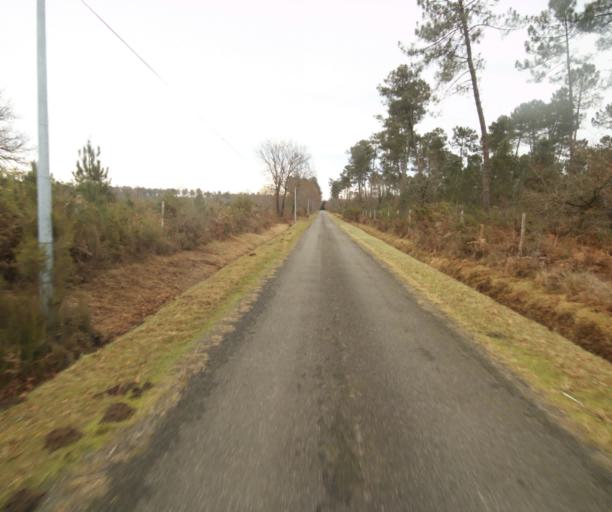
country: FR
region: Midi-Pyrenees
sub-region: Departement du Gers
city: Cazaubon
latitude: 44.0209
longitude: -0.0746
